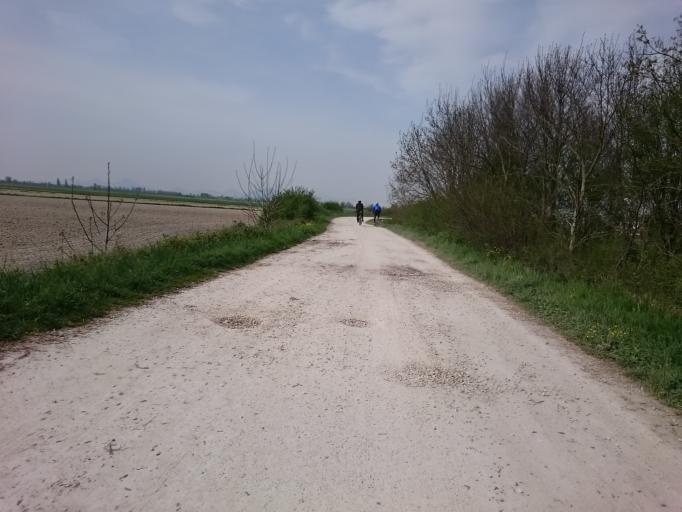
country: IT
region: Veneto
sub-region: Provincia di Padova
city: Tribano
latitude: 45.1784
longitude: 11.8431
